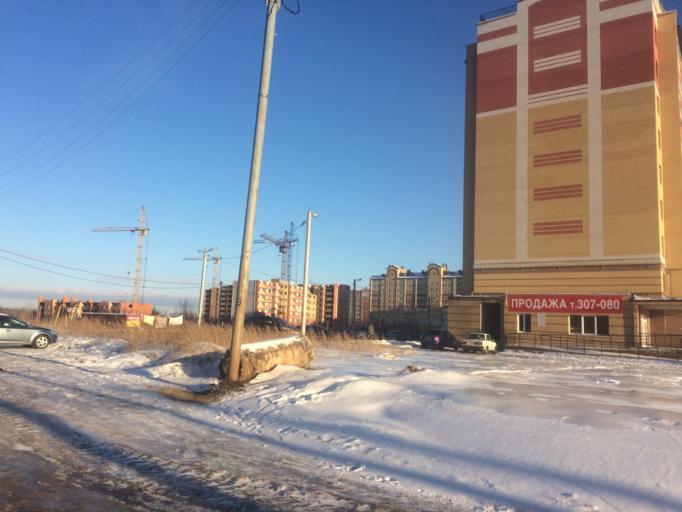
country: RU
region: Mariy-El
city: Yoshkar-Ola
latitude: 56.6407
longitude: 47.9194
